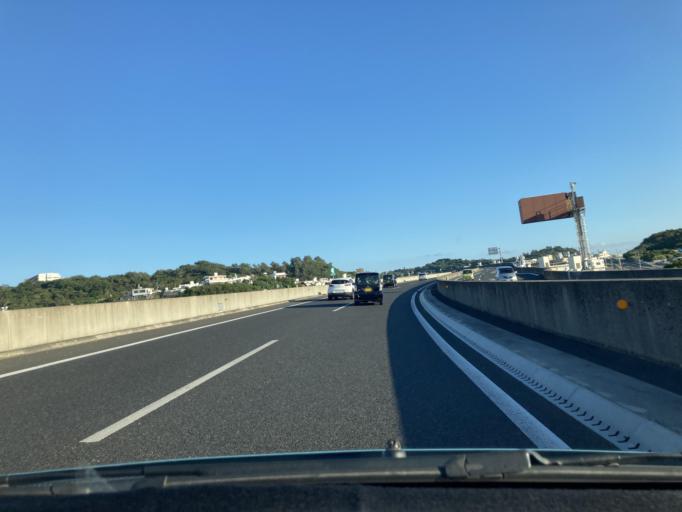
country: JP
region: Okinawa
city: Tomigusuku
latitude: 26.1747
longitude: 127.6748
